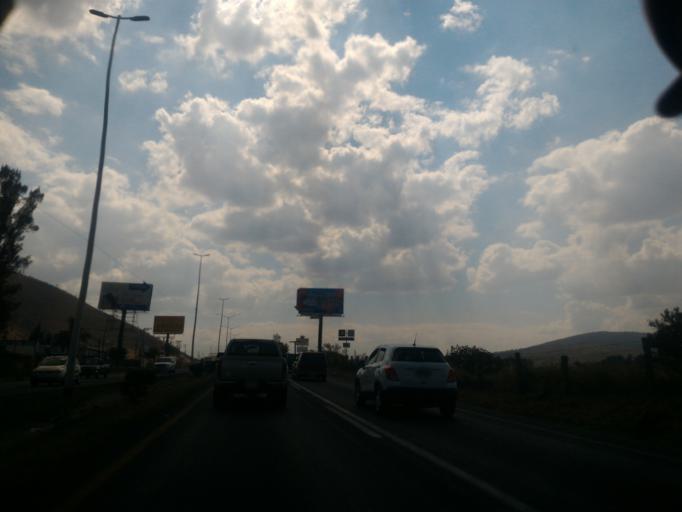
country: MX
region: Jalisco
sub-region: Tlajomulco de Zuniga
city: Lomas de San Agustin
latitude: 20.5274
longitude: -103.4785
